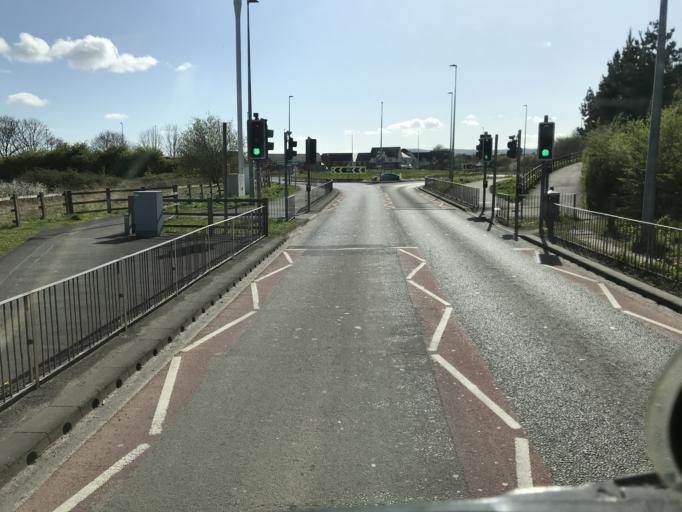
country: GB
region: Wales
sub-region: County of Flintshire
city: Hawarden
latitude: 53.1675
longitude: -2.9777
